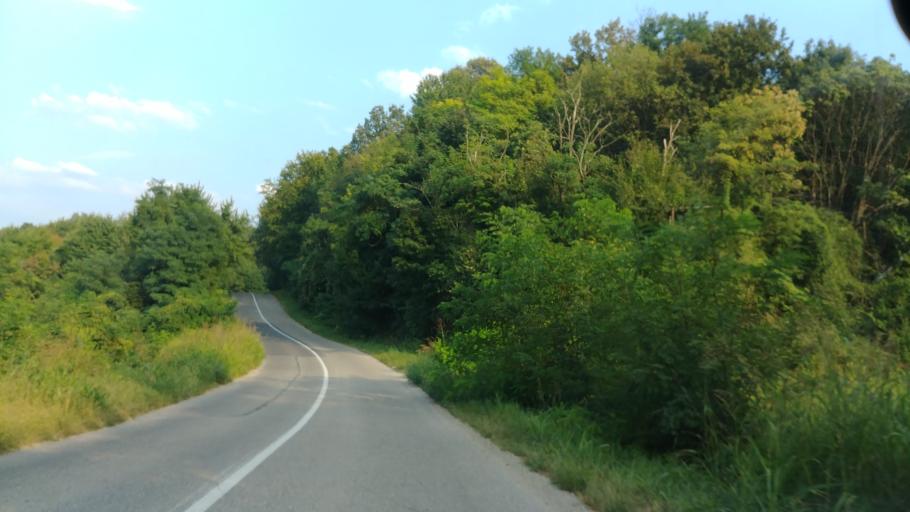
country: BA
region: Republika Srpska
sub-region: Opstina Ugljevik
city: Ugljevik
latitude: 44.7062
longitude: 18.9610
